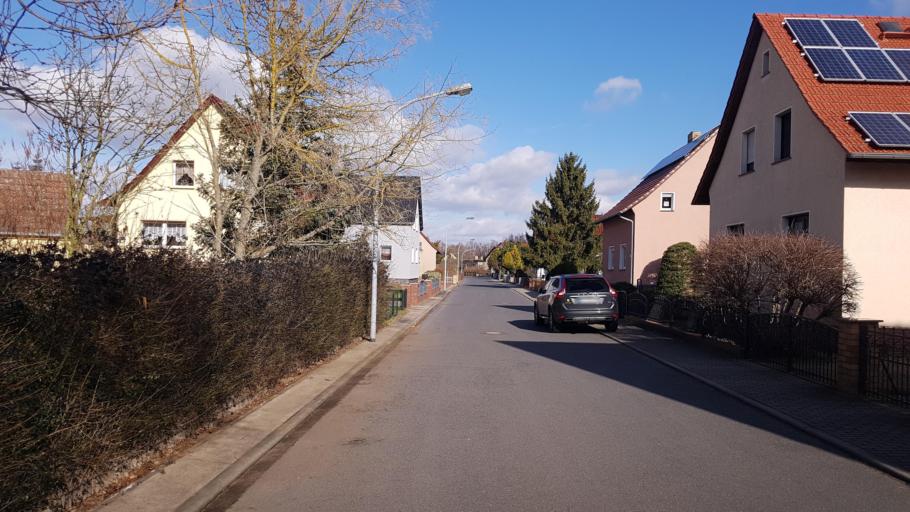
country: DE
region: Brandenburg
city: Herzberg
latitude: 51.6980
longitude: 13.2295
